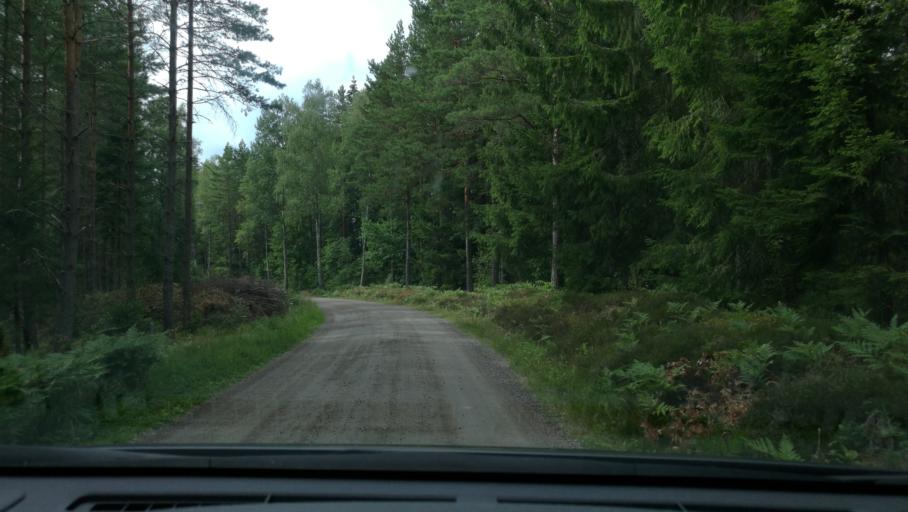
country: SE
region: OEstergoetland
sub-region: Norrkopings Kommun
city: Svartinge
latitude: 58.7560
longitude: 15.9539
